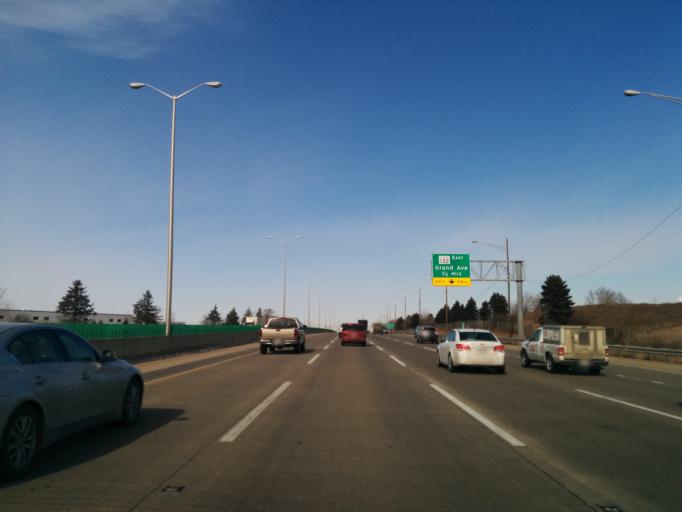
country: US
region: Illinois
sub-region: Lake County
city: Gurnee
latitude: 42.3692
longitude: -87.9416
